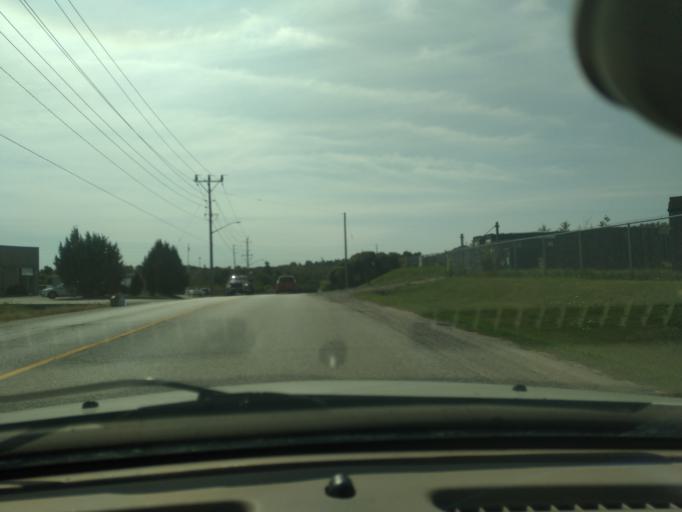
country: CA
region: Ontario
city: Innisfil
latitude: 44.3265
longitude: -79.6762
